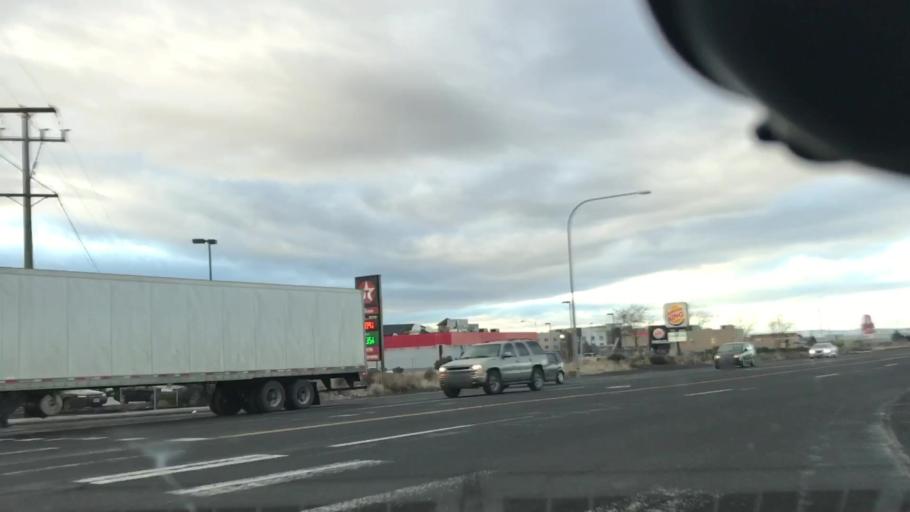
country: US
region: Washington
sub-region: Grant County
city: Moses Lake
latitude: 47.1017
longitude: -119.2465
